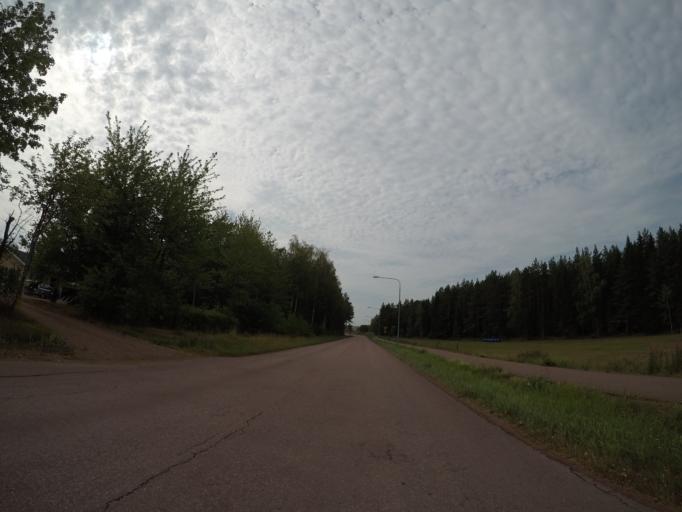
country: AX
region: Alands landsbygd
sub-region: Finstroem
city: Finstroem
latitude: 60.2180
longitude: 19.9796
